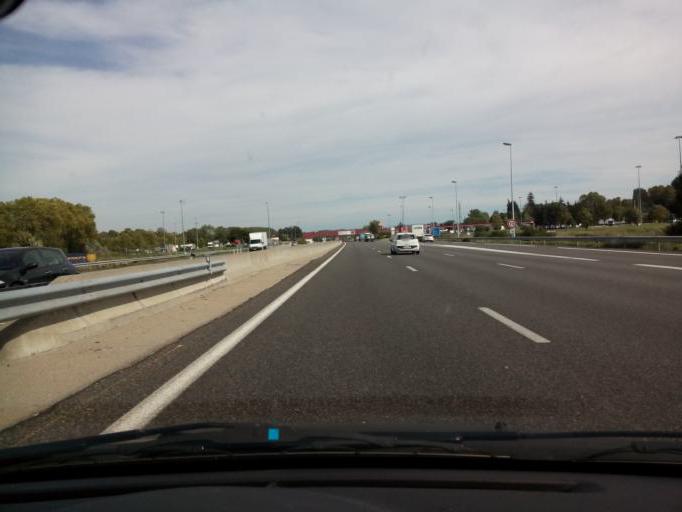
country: FR
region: Rhone-Alpes
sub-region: Departement de l'Isere
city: Vaulx-Milieu
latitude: 45.6136
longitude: 5.2052
